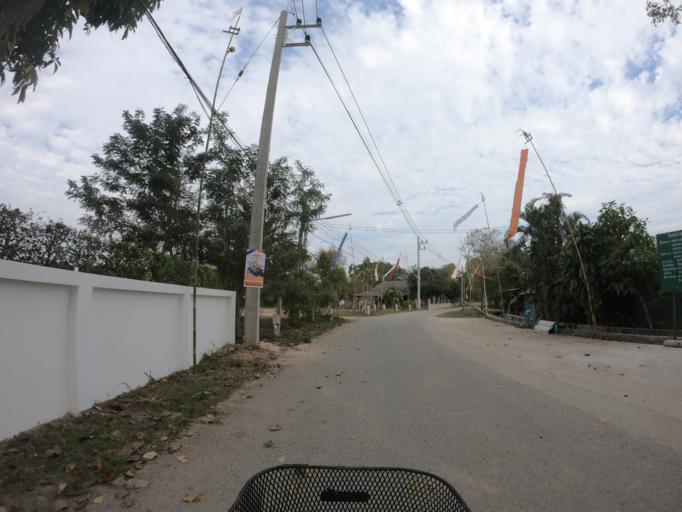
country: TH
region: Chiang Mai
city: San Sai
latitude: 18.7959
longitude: 99.0539
